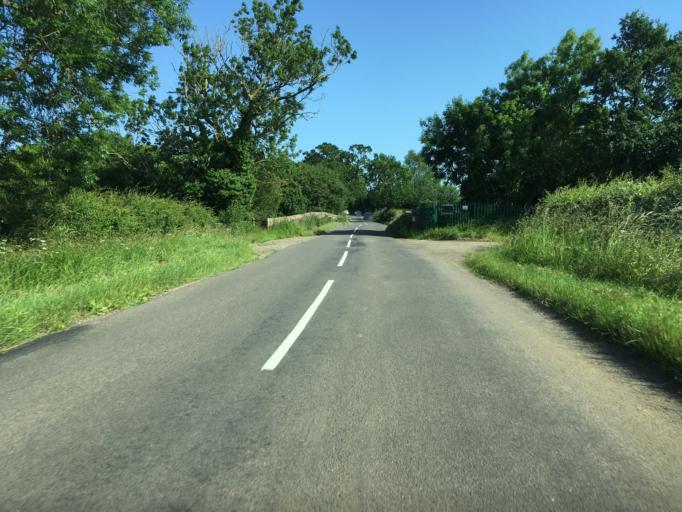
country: GB
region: England
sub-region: Buckinghamshire
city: Steeple Claydon
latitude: 51.9399
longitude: -0.9439
